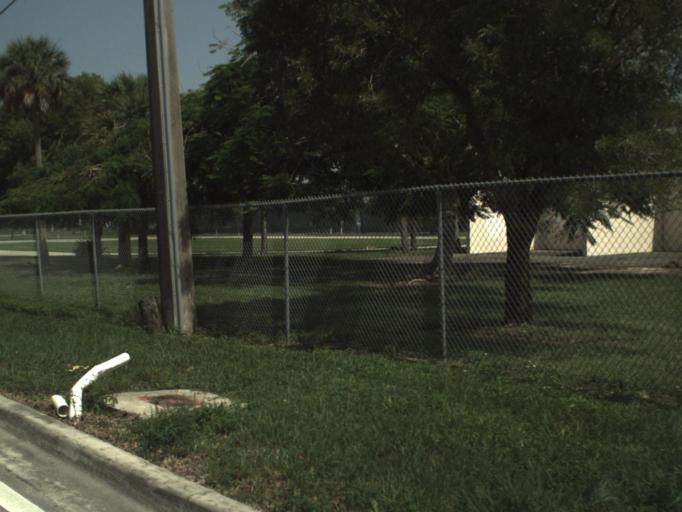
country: US
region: Florida
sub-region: Broward County
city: Coral Springs
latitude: 26.2728
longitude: -80.2937
